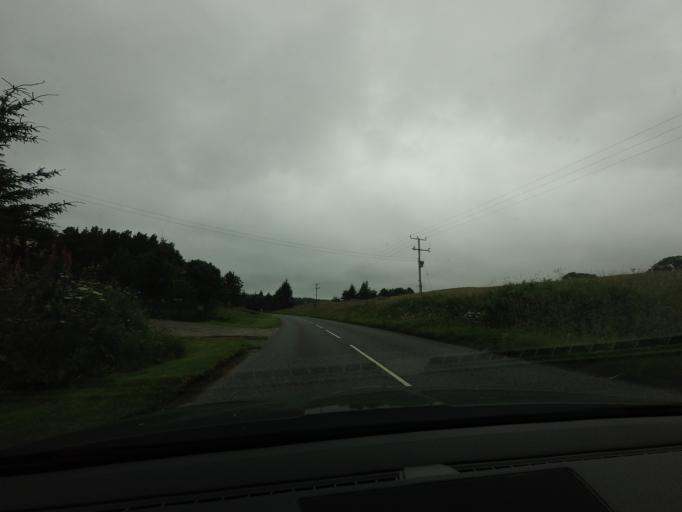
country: GB
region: Scotland
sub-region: Highland
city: Alness
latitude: 58.0078
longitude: -4.3954
